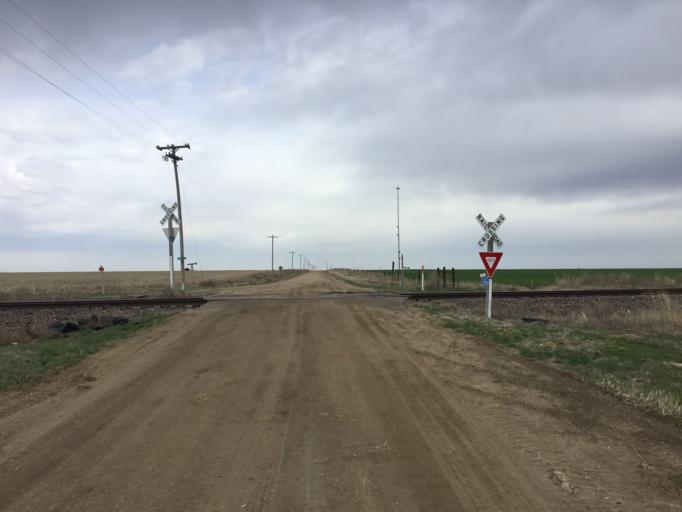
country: US
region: Kansas
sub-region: Russell County
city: Russell
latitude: 38.8856
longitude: -98.9102
